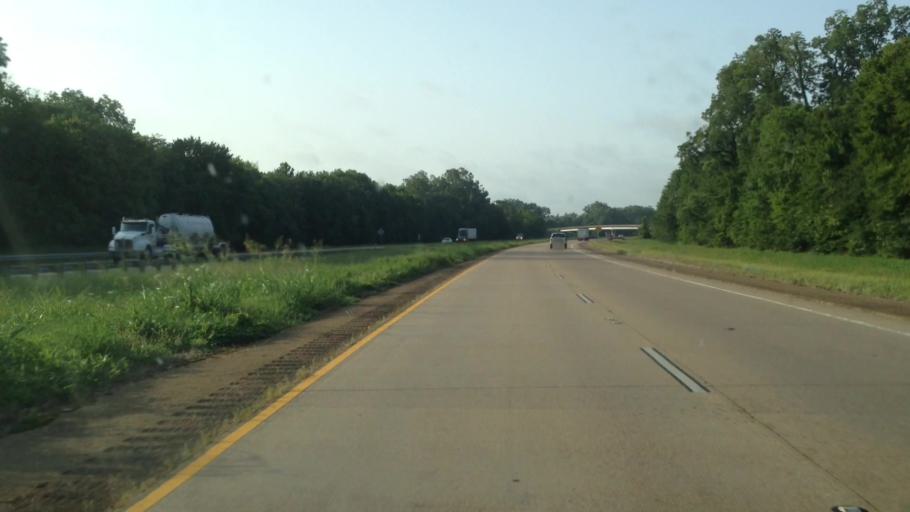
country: US
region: Louisiana
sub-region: Rapides Parish
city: Woodworth
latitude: 31.1319
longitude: -92.4457
